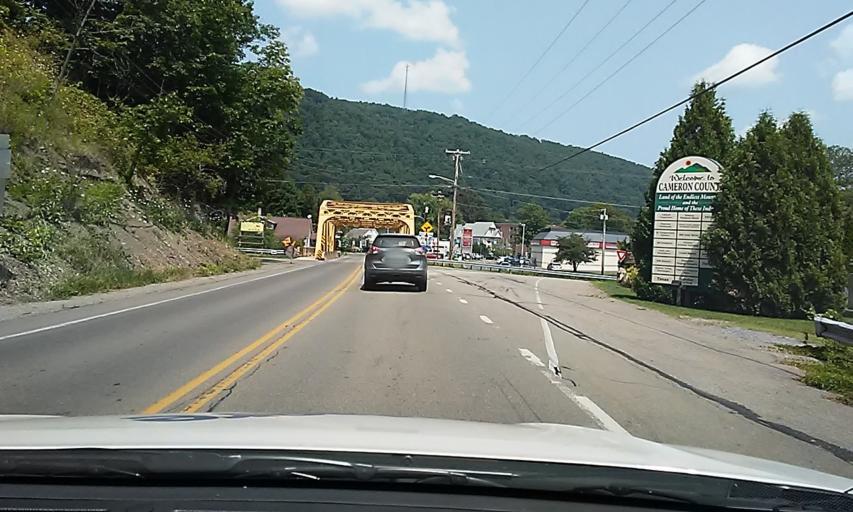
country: US
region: Pennsylvania
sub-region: Cameron County
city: Emporium
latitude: 41.5098
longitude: -78.2478
